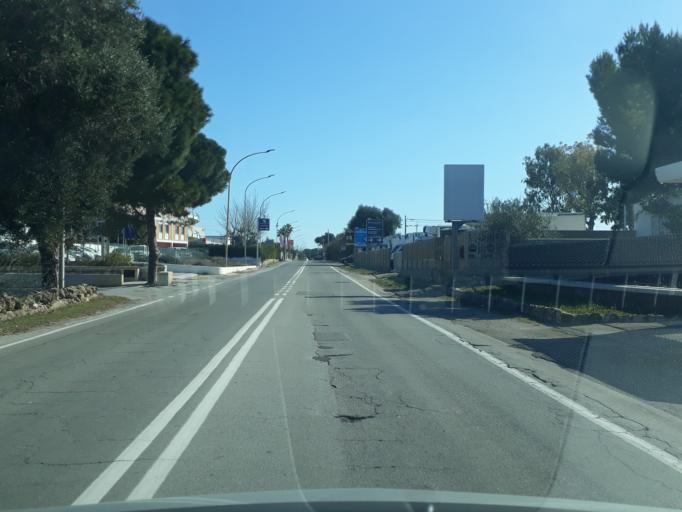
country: IT
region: Apulia
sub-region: Provincia di Bari
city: Monopoli
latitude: 40.9655
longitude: 17.2744
